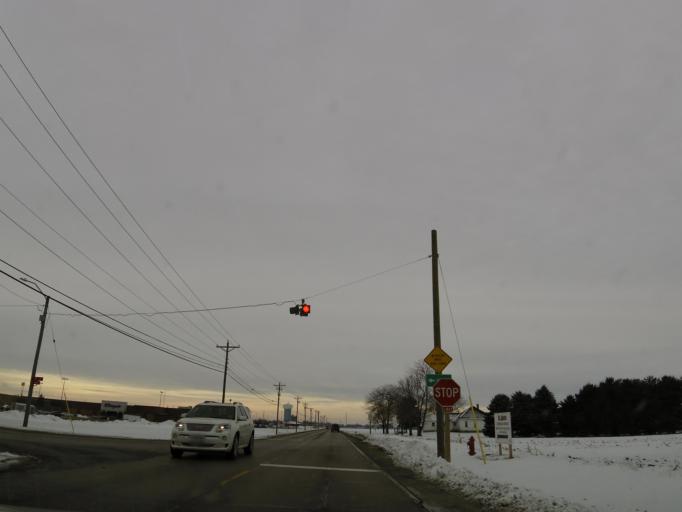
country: US
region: Illinois
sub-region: LaSalle County
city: Peru
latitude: 41.3583
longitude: -89.1302
